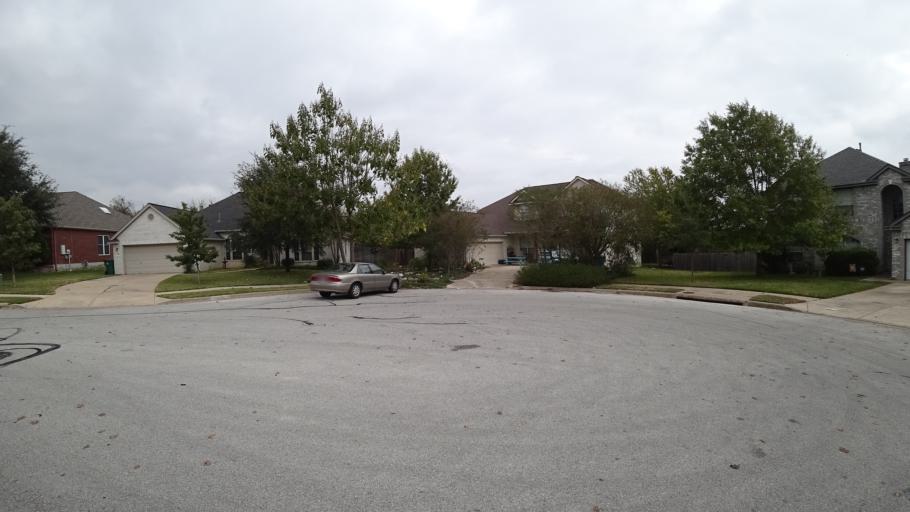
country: US
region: Texas
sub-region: Travis County
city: Pflugerville
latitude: 30.4421
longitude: -97.6030
